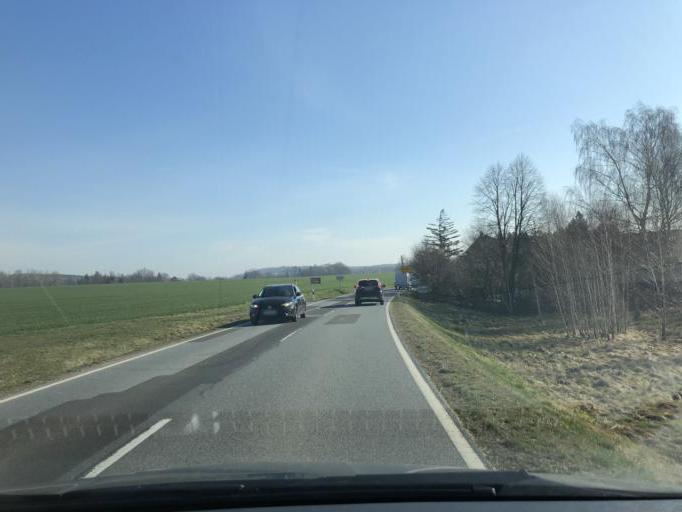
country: DE
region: Saxony
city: Rammenau
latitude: 51.1529
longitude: 14.1203
